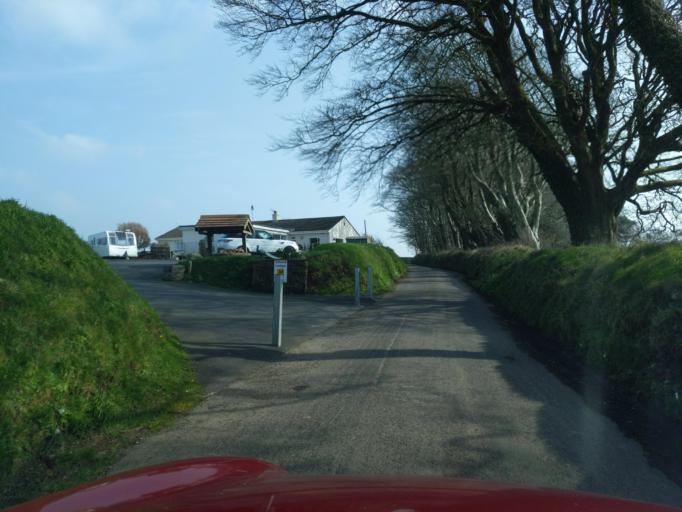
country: GB
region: England
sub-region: Devon
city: Kingsbridge
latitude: 50.3097
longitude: -3.7704
